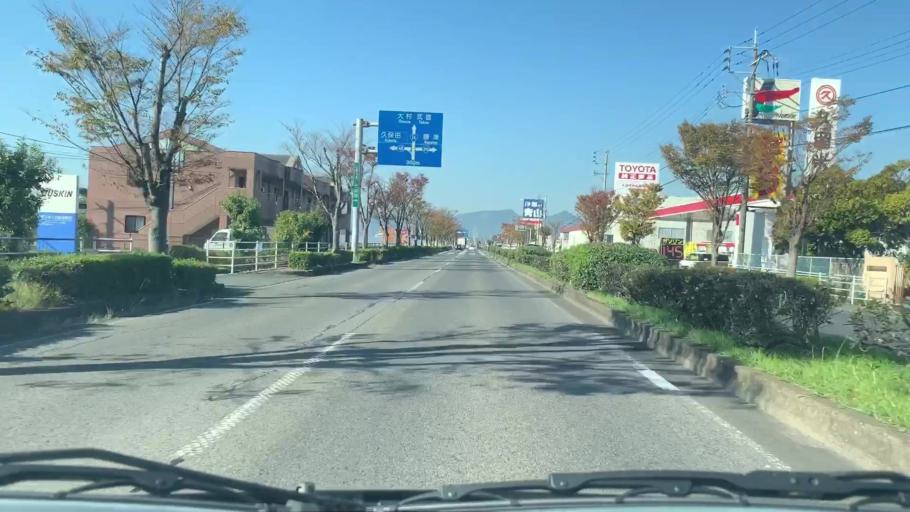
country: JP
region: Saga Prefecture
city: Saga-shi
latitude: 33.2631
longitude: 130.2343
